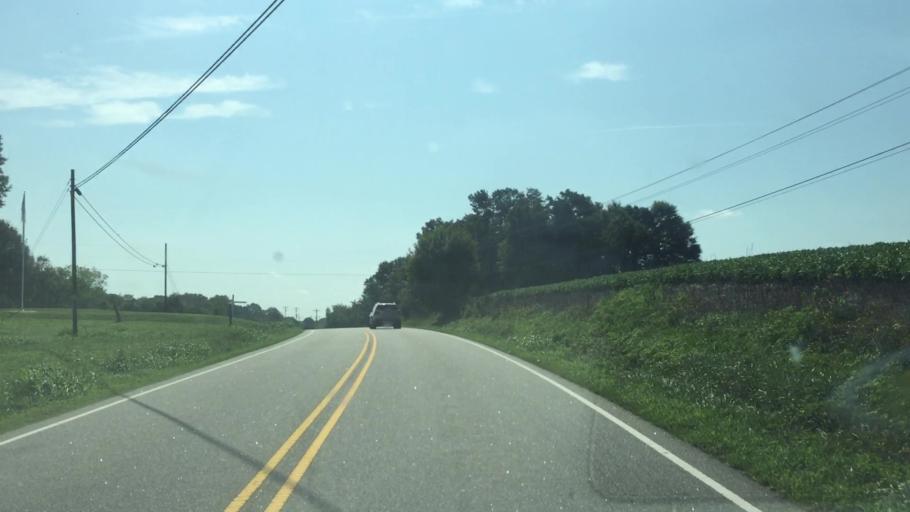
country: US
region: North Carolina
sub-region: Union County
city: Unionville
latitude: 35.1343
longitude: -80.4553
